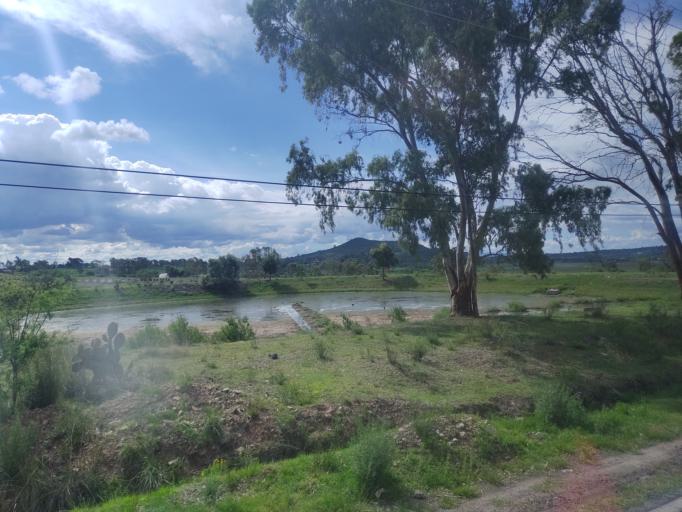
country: MX
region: Mexico
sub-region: Aculco
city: El Colorado
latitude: 20.1009
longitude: -99.7384
